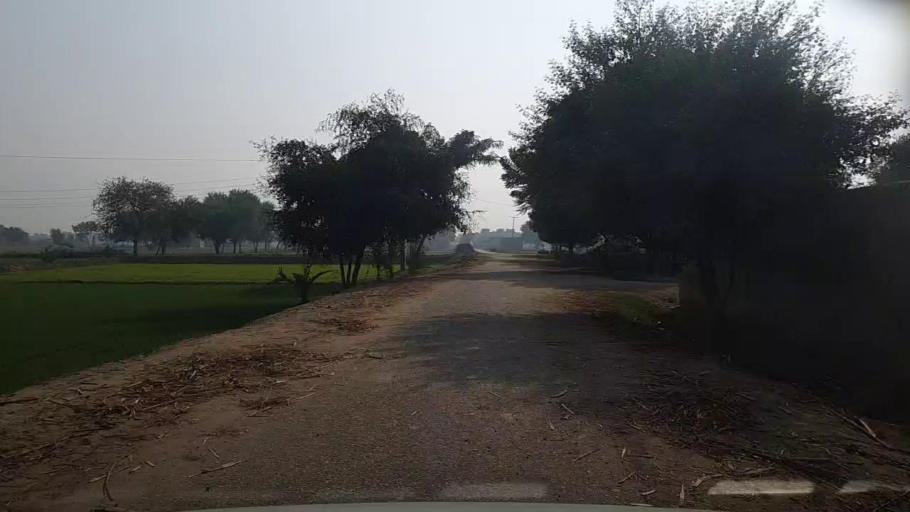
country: PK
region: Sindh
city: Setharja Old
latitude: 27.1226
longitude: 68.5159
